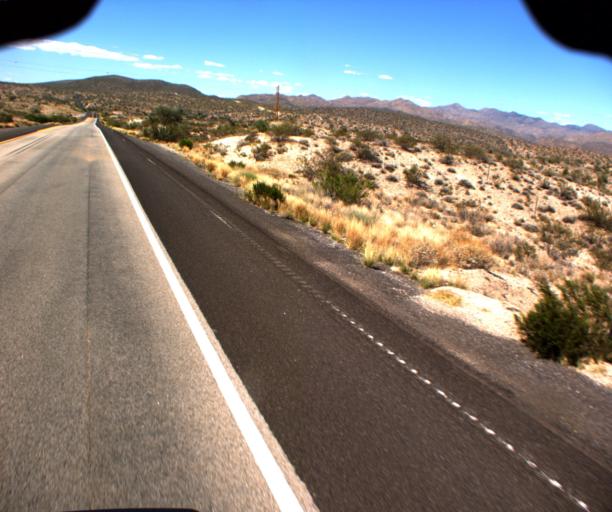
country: US
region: Arizona
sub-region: Mohave County
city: Kingman
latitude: 34.9061
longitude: -113.6562
